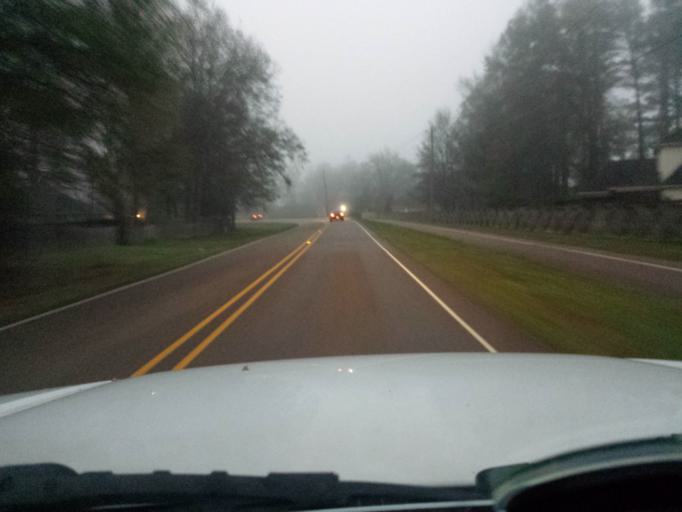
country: US
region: Mississippi
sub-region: Madison County
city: Madison
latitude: 32.4161
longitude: -90.0208
